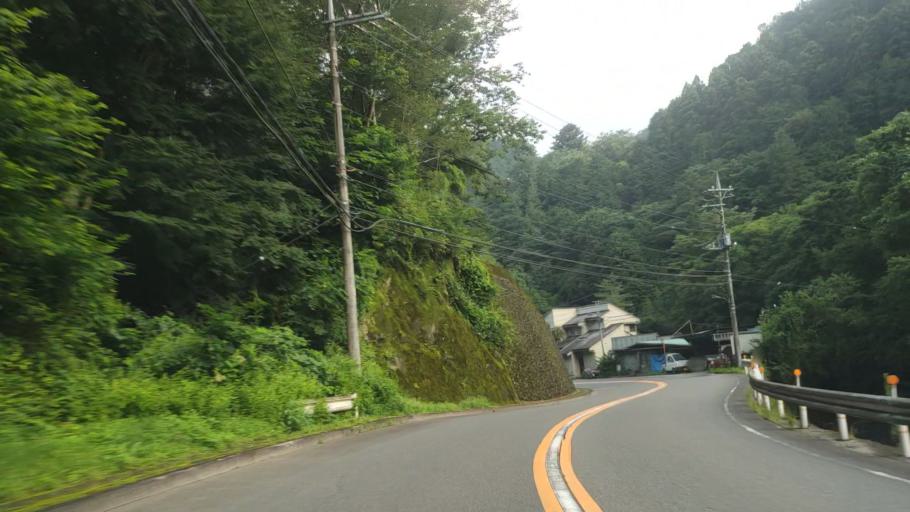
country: JP
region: Tokyo
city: Ome
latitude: 35.8327
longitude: 139.2256
